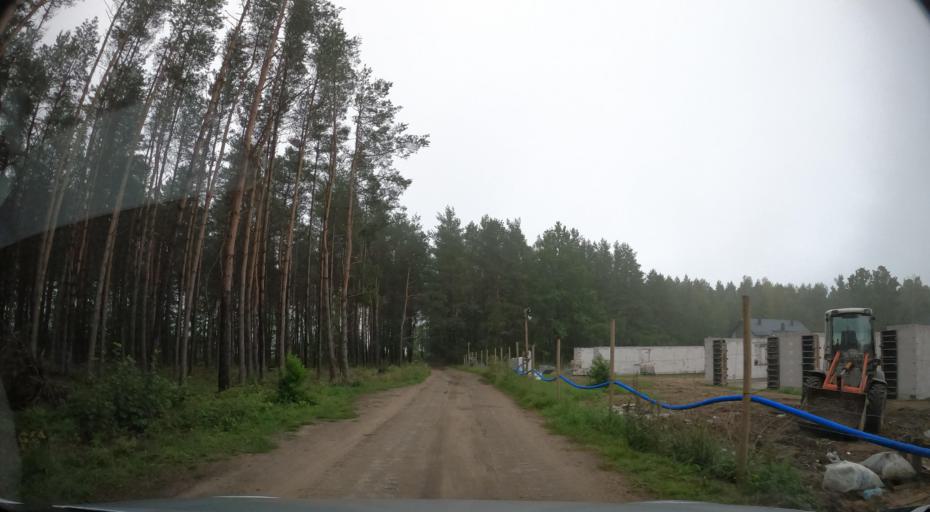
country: PL
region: Pomeranian Voivodeship
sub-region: Powiat kartuski
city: Chwaszczyno
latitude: 54.4358
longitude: 18.4161
